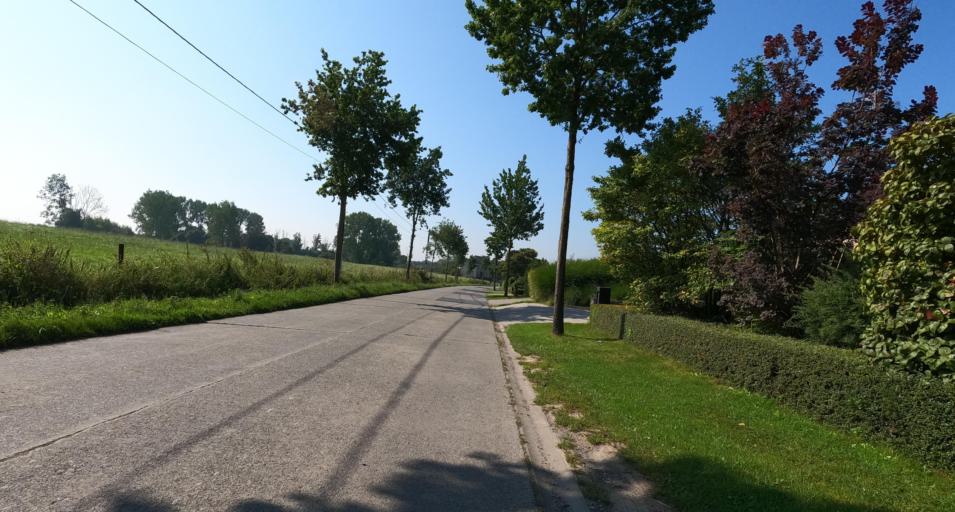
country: BE
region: Flanders
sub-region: Provincie Oost-Vlaanderen
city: Temse
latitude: 51.1390
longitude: 4.2148
